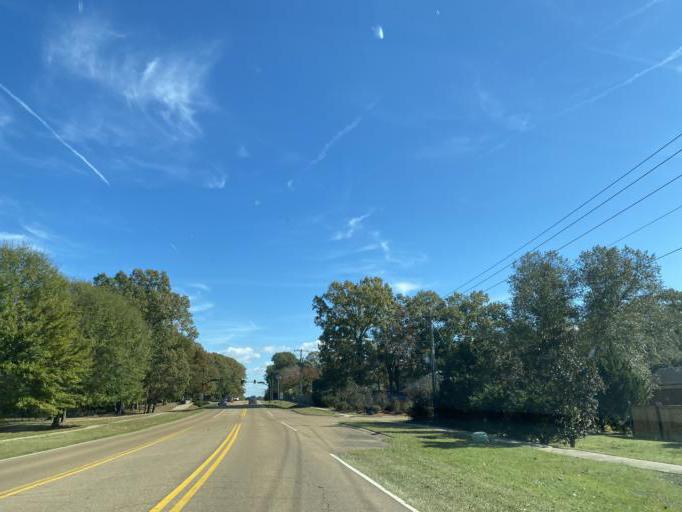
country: US
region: Mississippi
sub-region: Madison County
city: Madison
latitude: 32.4575
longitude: -90.1034
